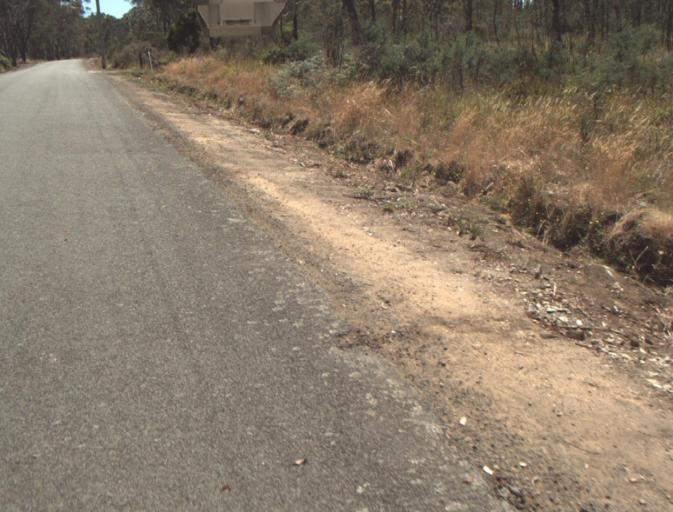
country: AU
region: Tasmania
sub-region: Launceston
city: Newstead
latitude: -41.3874
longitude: 147.2966
